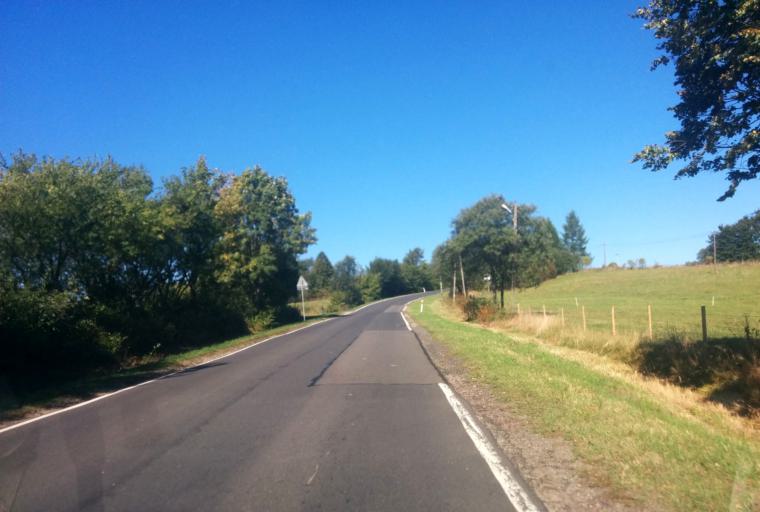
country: PL
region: Subcarpathian Voivodeship
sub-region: Powiat bieszczadzki
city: Lutowiska
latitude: 49.2577
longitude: 22.6856
